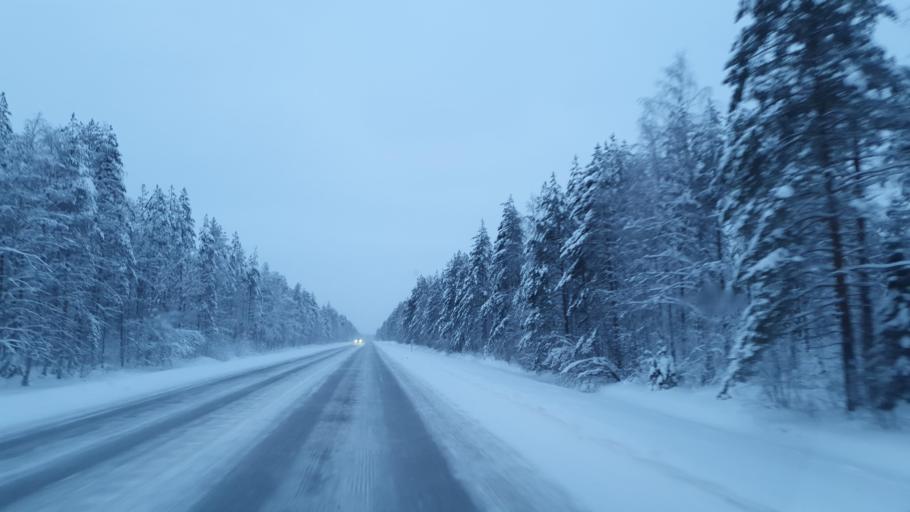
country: FI
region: Kainuu
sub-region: Kajaani
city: Vaala
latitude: 64.5976
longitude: 26.7311
